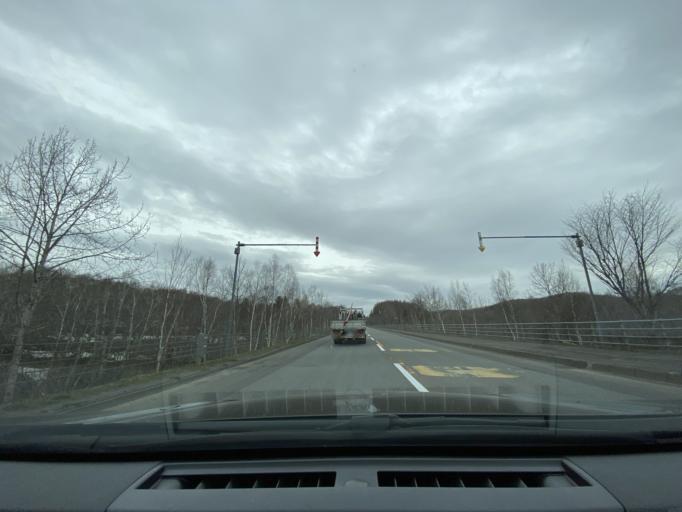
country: JP
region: Hokkaido
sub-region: Asahikawa-shi
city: Asahikawa
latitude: 43.9561
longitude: 142.4513
